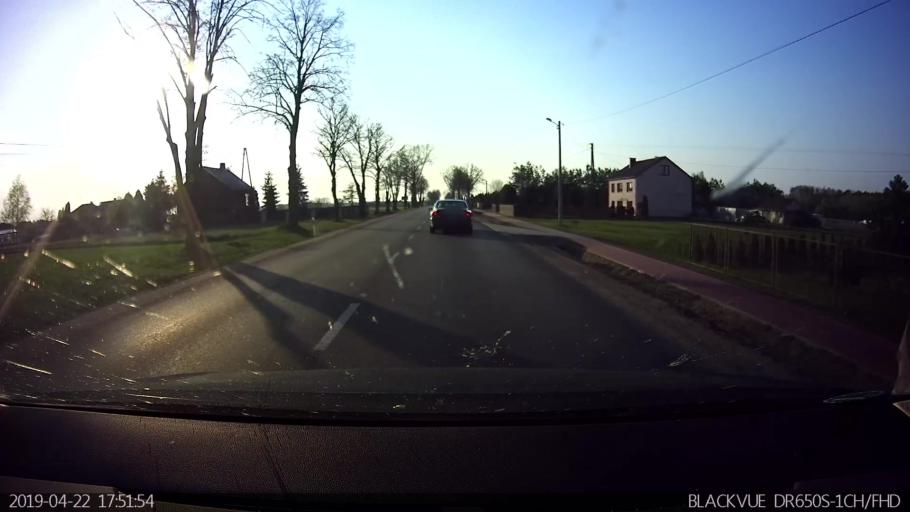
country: PL
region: Masovian Voivodeship
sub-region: Powiat wegrowski
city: Wegrow
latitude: 52.4376
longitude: 21.9881
